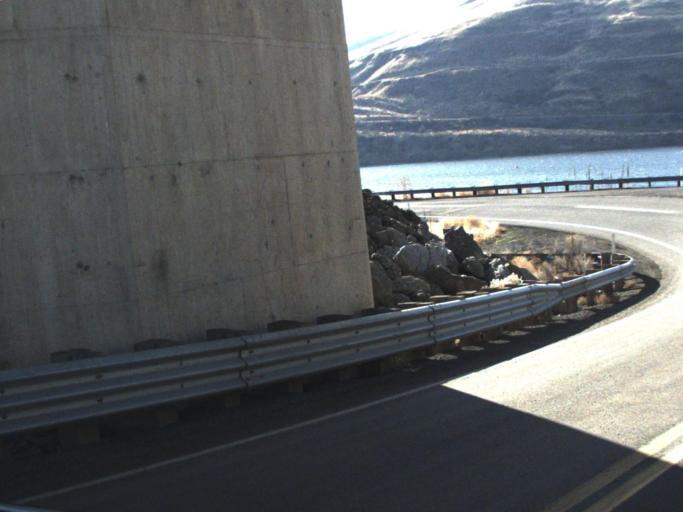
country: US
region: Washington
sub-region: Whitman County
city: Colfax
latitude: 46.7029
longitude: -117.4676
